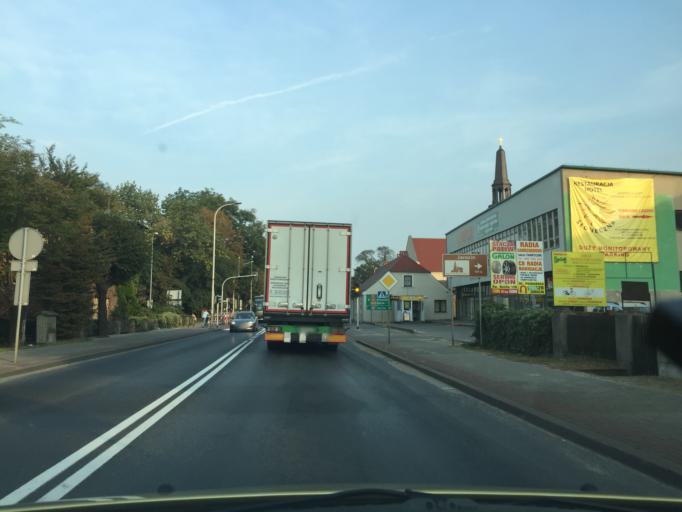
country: PL
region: Greater Poland Voivodeship
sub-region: Powiat jarocinski
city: Jarocin
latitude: 51.9744
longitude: 17.4992
